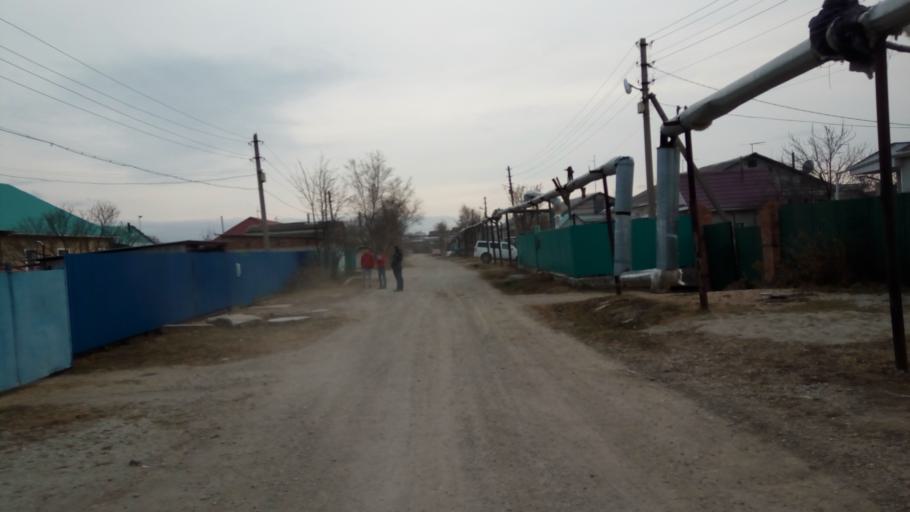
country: RU
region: Primorskiy
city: Novoshakhtinskiy
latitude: 44.0254
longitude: 132.1774
